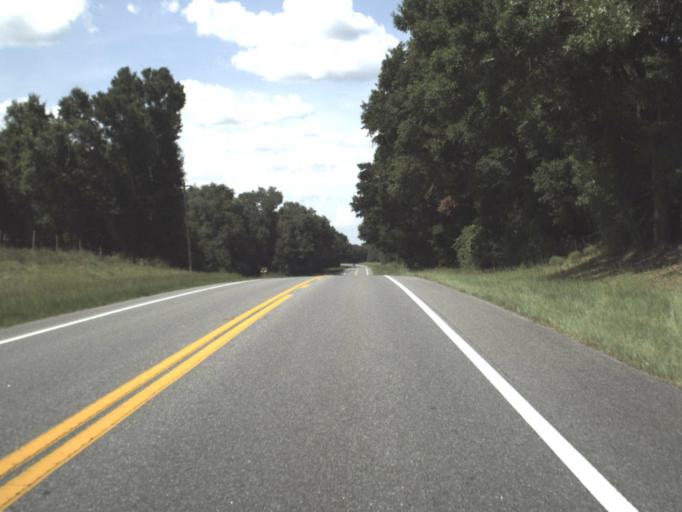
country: US
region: Florida
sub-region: Gilchrist County
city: Trenton
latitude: 29.7309
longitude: -82.7443
